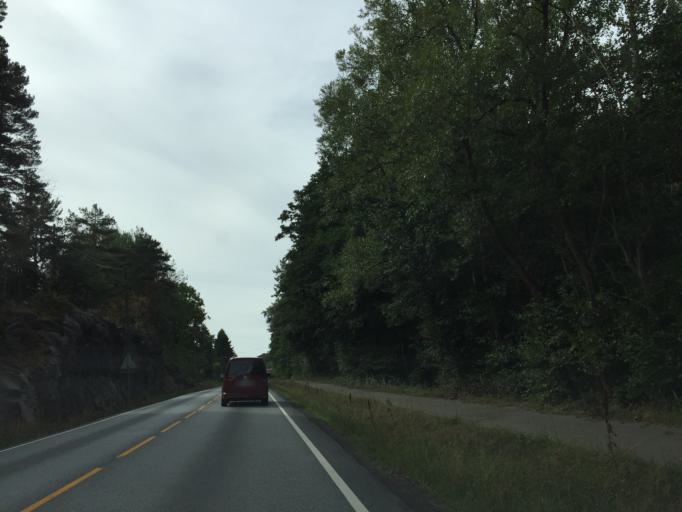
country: NO
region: Ostfold
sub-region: Fredrikstad
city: Fredrikstad
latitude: 59.1092
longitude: 10.9089
